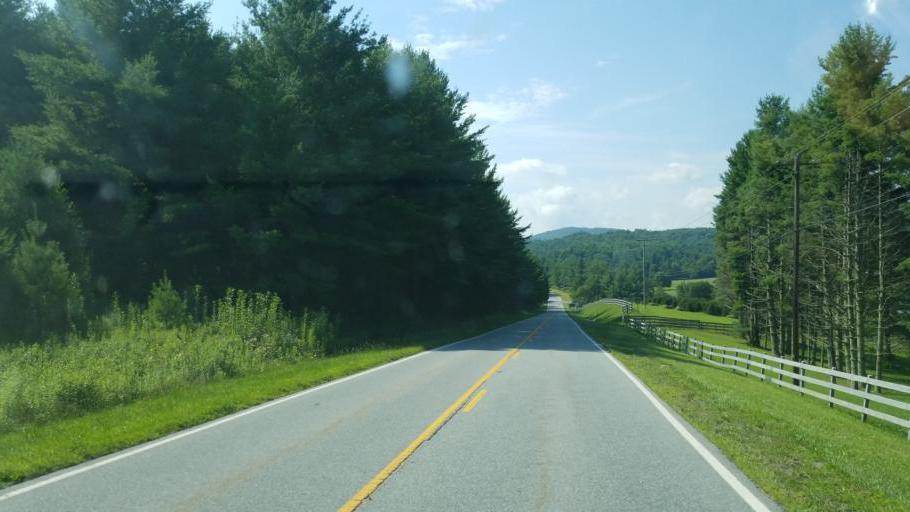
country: US
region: North Carolina
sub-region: Avery County
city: Newland
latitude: 36.0121
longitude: -81.8949
